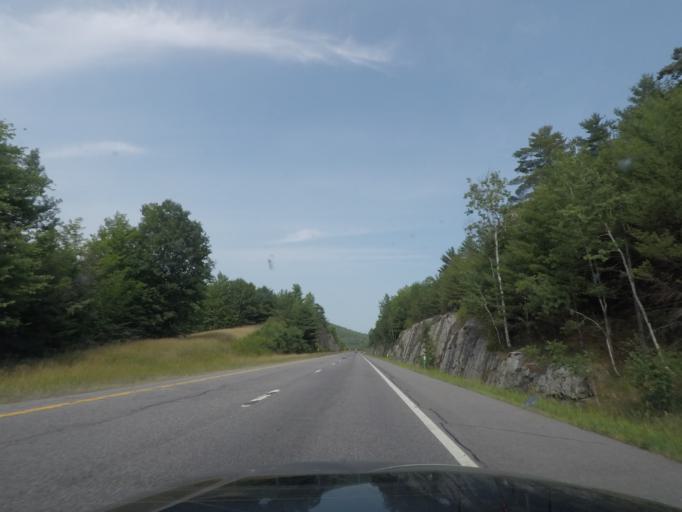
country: US
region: New York
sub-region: Essex County
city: Elizabethtown
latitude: 44.1926
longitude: -73.5414
